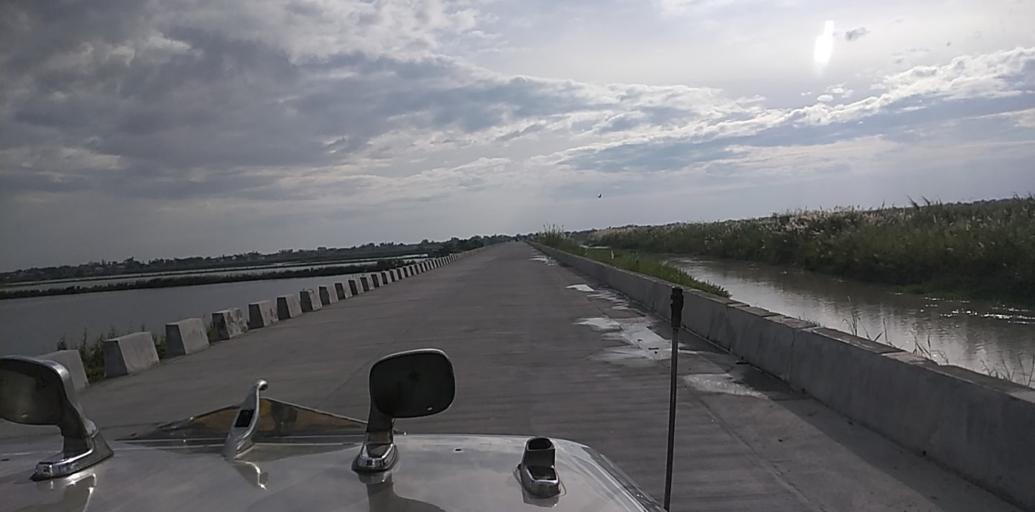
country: PH
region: Central Luzon
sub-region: Province of Pampanga
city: Minalin
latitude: 14.9752
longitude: 120.6806
